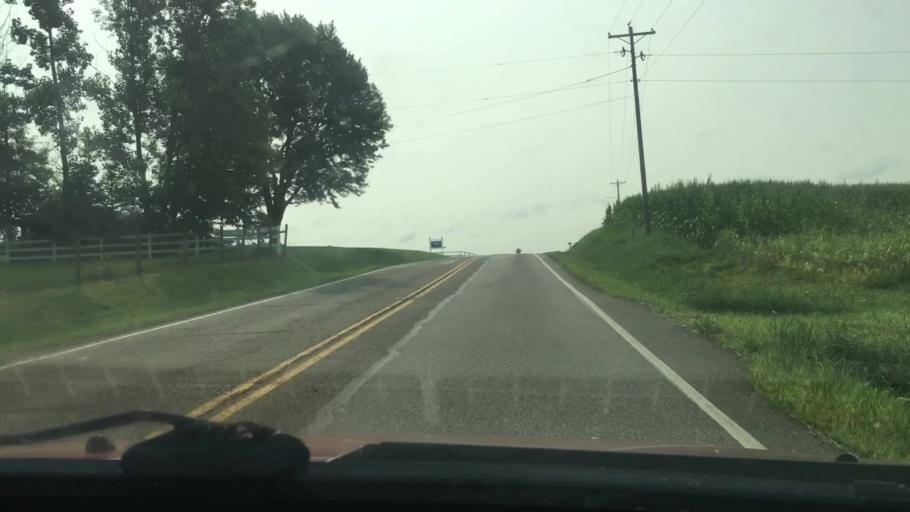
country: US
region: Ohio
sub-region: Belmont County
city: Barnesville
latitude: 40.1510
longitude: -81.2333
